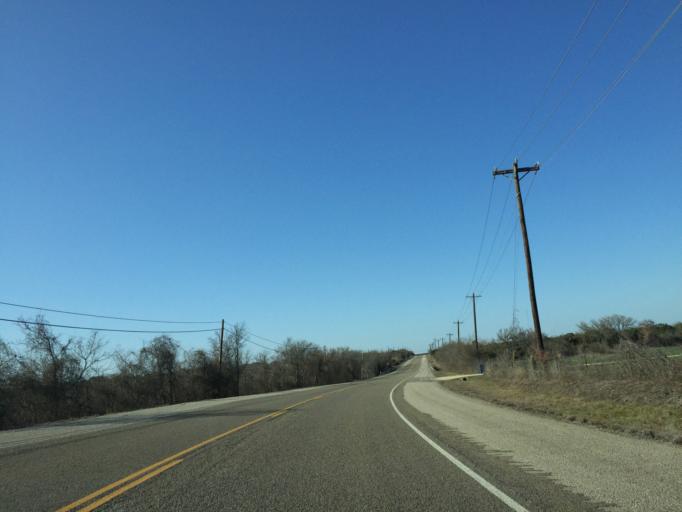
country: US
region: Texas
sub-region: Williamson County
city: Florence
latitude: 30.7660
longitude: -97.8456
